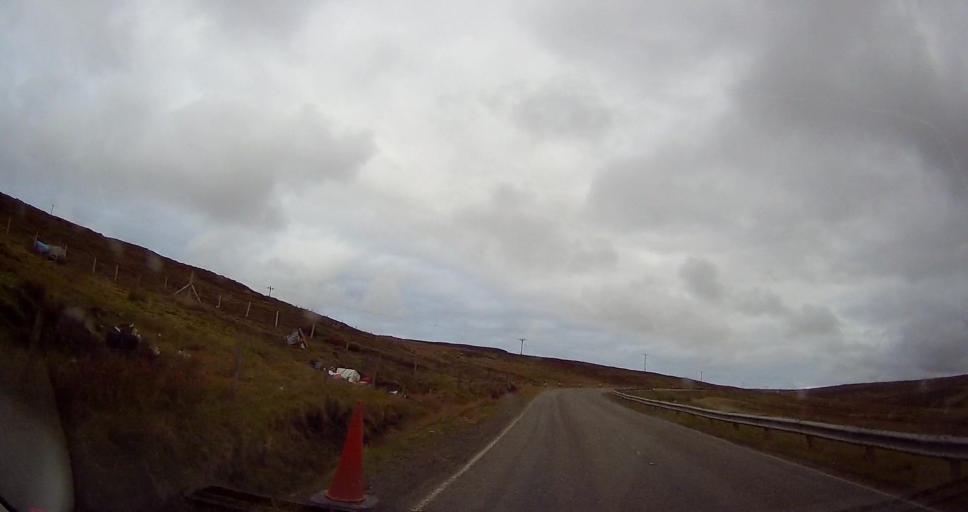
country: GB
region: Scotland
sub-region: Shetland Islands
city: Shetland
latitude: 60.6127
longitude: -1.0738
